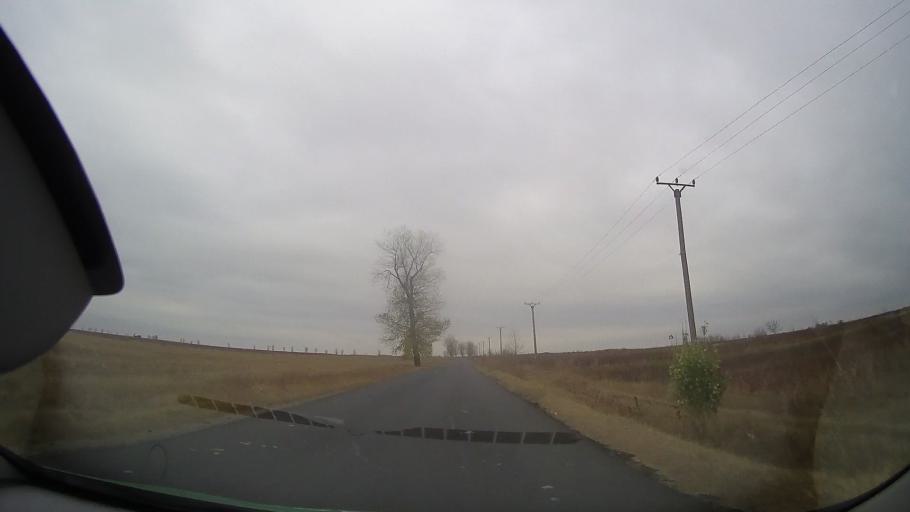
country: RO
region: Braila
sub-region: Comuna Ciresu
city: Ciresu
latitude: 44.9407
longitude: 27.3543
